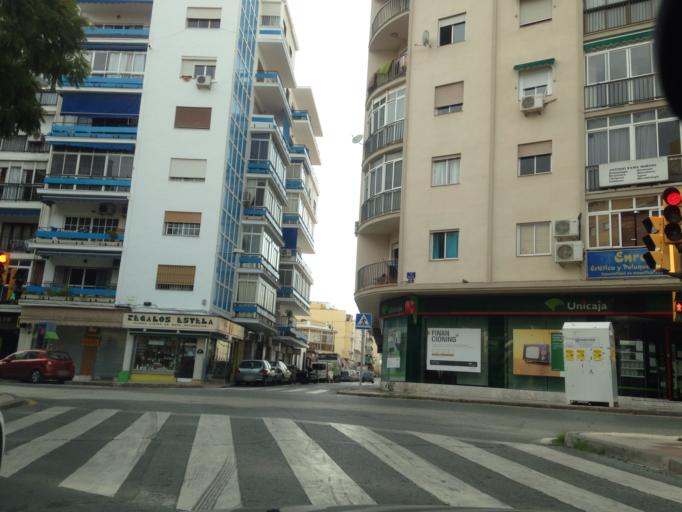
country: ES
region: Andalusia
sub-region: Provincia de Malaga
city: Malaga
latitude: 36.7243
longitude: -4.4317
